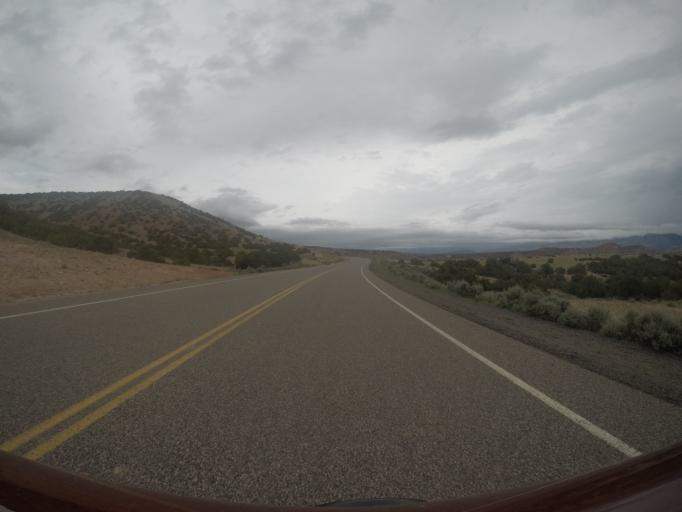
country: US
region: Wyoming
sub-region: Big Horn County
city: Lovell
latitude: 45.0682
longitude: -108.2552
